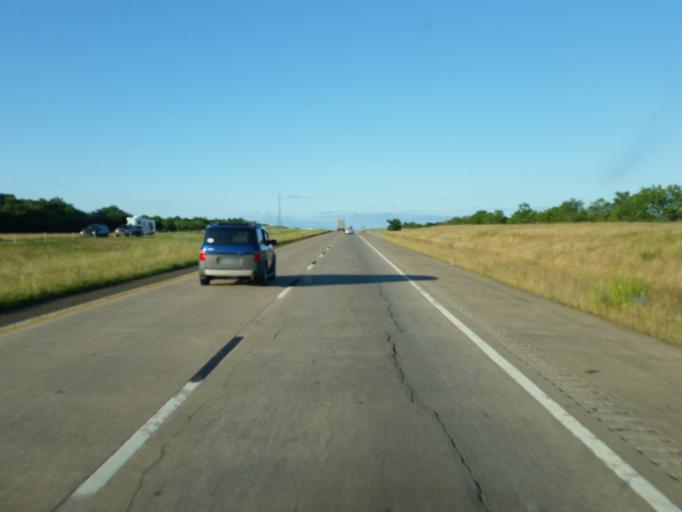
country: US
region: Texas
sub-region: Kaufman County
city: Talty
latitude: 32.7052
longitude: -96.3507
